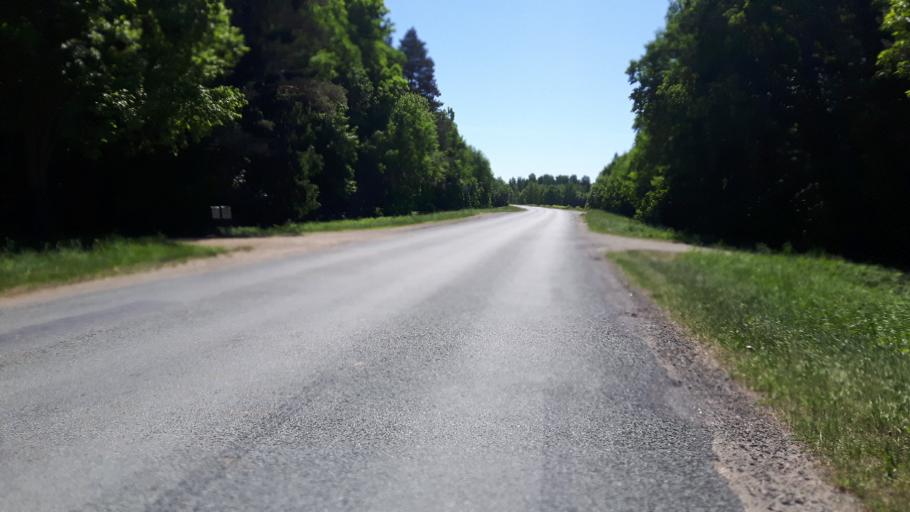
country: EE
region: Harju
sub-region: Kuusalu vald
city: Kuusalu
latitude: 59.4681
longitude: 25.4492
